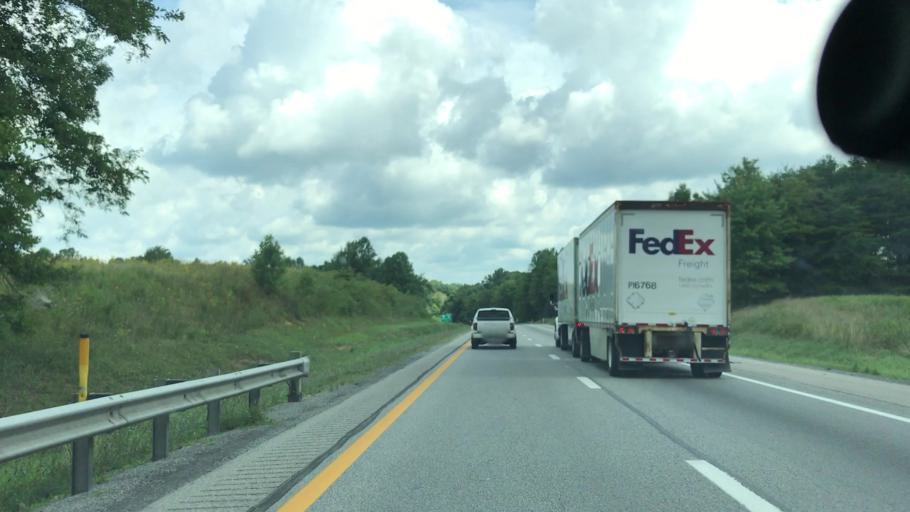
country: US
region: West Virginia
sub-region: Mercer County
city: Athens
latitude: 37.4029
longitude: -81.0614
